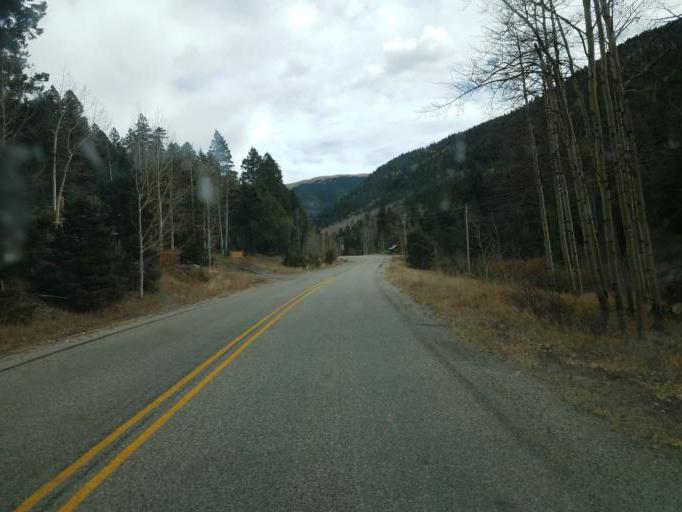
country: US
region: New Mexico
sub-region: Taos County
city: Arroyo Seco
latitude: 36.5957
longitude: -105.4745
